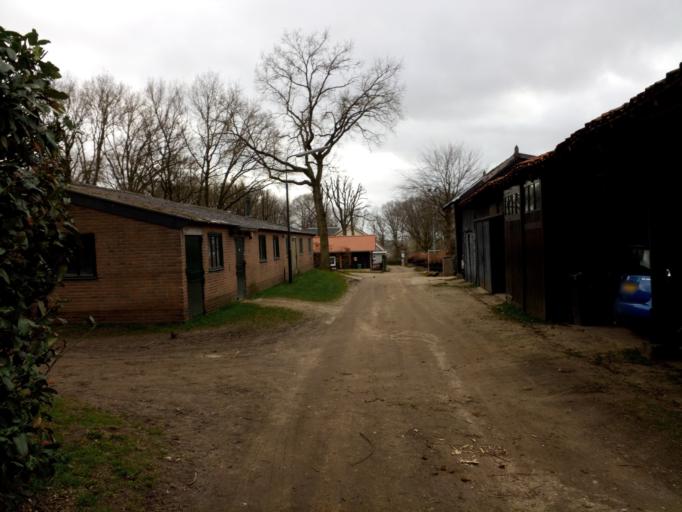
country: NL
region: Utrecht
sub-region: Gemeente Rhenen
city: Rhenen
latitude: 51.9690
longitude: 5.5495
